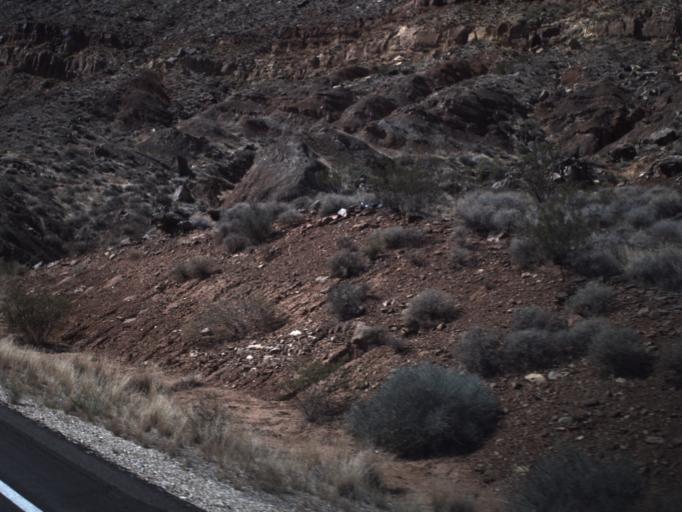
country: US
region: Utah
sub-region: Washington County
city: Hurricane
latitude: 37.1856
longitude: -113.3975
